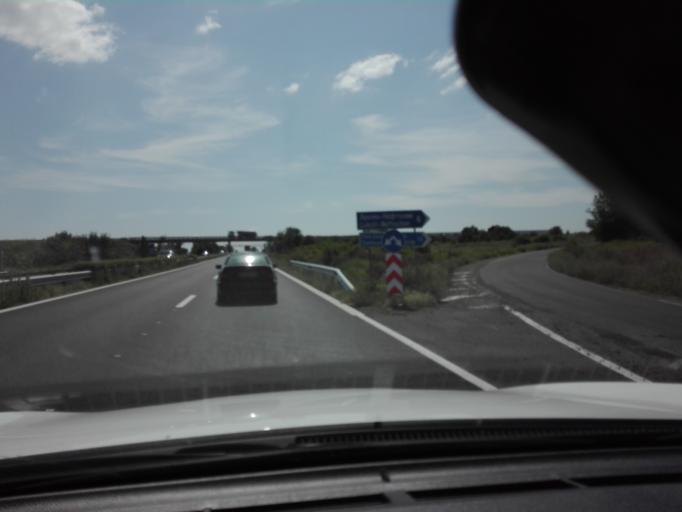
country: BG
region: Burgas
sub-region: Obshtina Burgas
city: Burgas
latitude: 42.5775
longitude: 27.4083
